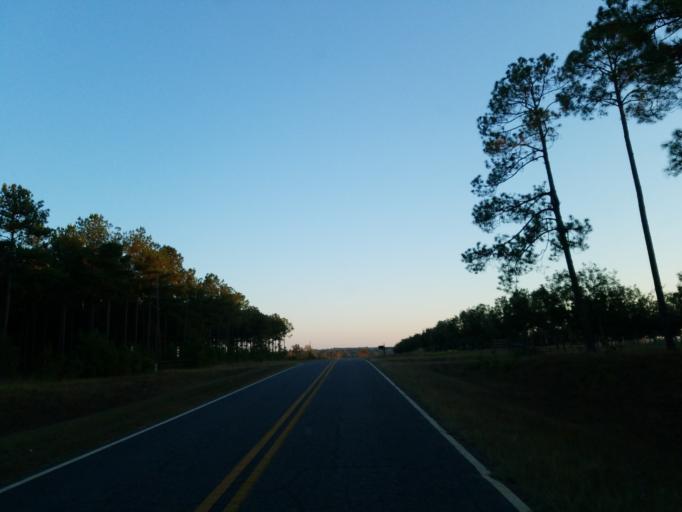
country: US
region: Georgia
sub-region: Ben Hill County
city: Fitzgerald
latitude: 31.6964
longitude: -83.4148
